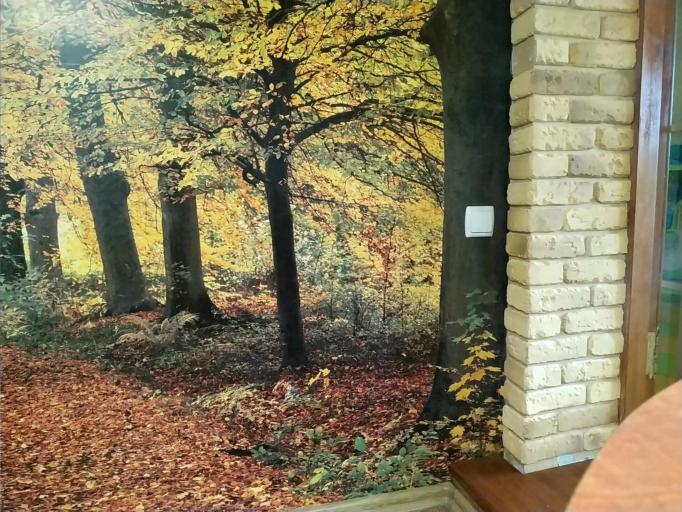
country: BY
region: Mogilev
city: Khotsimsk
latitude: 53.5465
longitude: 32.5104
